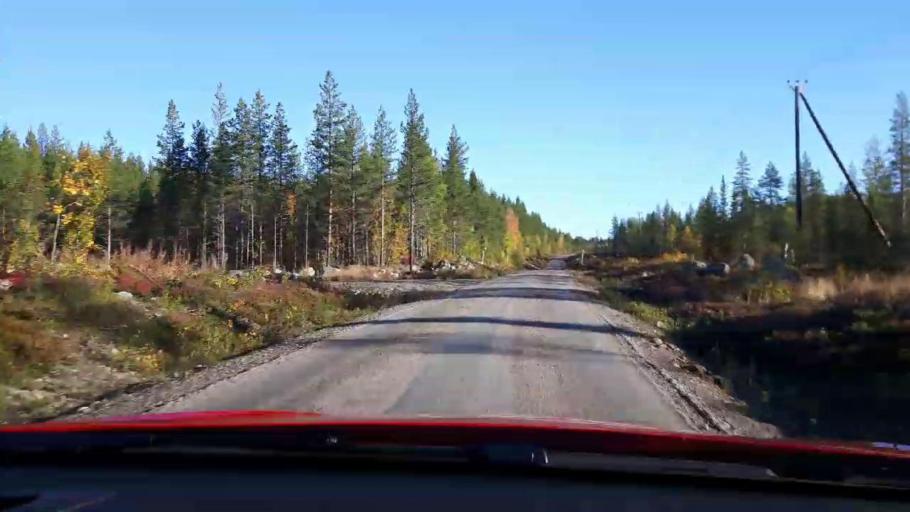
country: SE
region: Jaemtland
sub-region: Stroemsunds Kommun
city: Stroemsund
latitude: 64.3809
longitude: 15.1484
